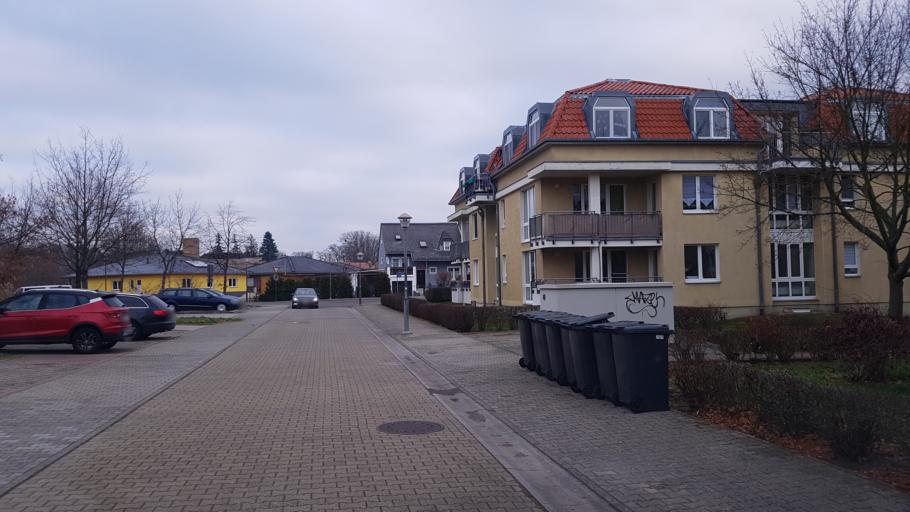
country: DE
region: Brandenburg
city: Schipkau
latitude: 51.5491
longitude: 13.9162
